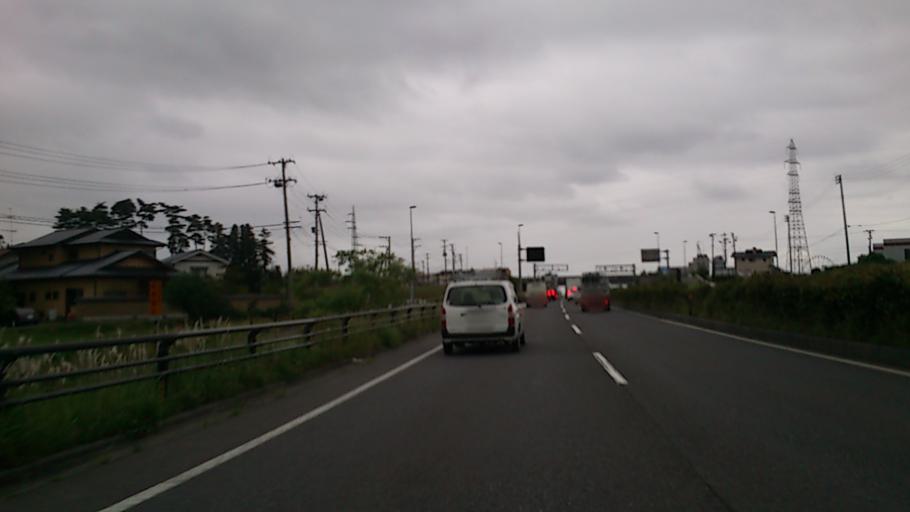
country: JP
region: Fukushima
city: Koriyama
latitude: 37.4544
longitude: 140.3786
